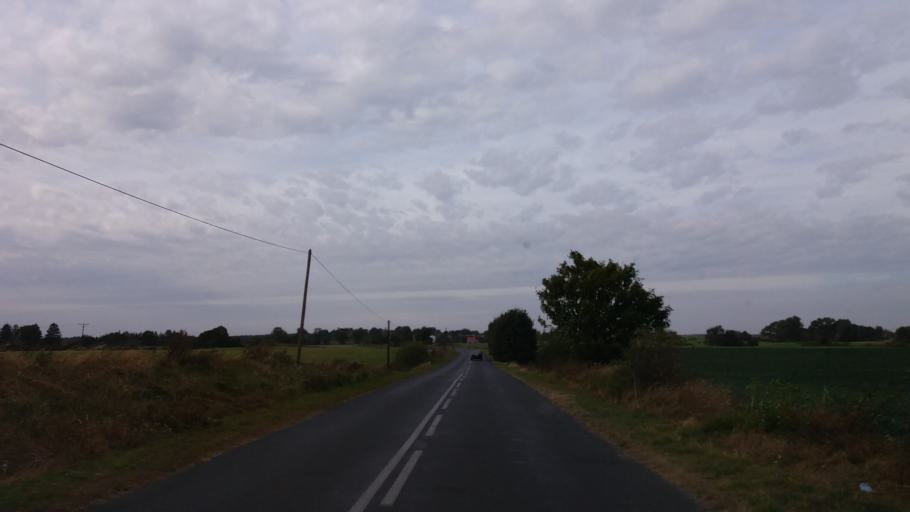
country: PL
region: Lubusz
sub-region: Powiat strzelecko-drezdenecki
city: Strzelce Krajenskie
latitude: 52.9169
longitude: 15.4921
